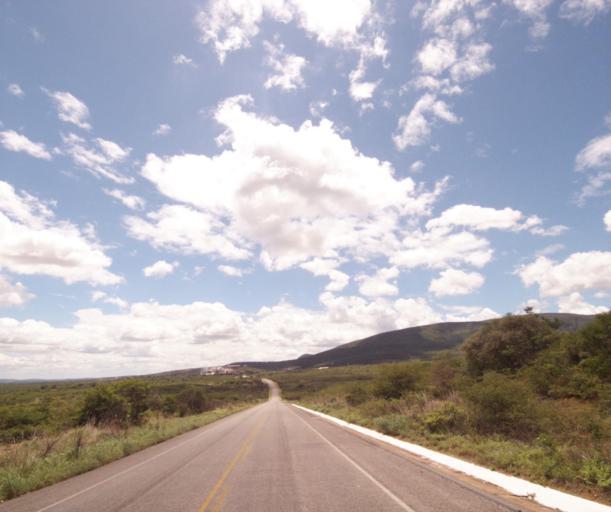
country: BR
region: Bahia
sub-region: Brumado
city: Brumado
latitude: -14.2367
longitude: -41.7023
